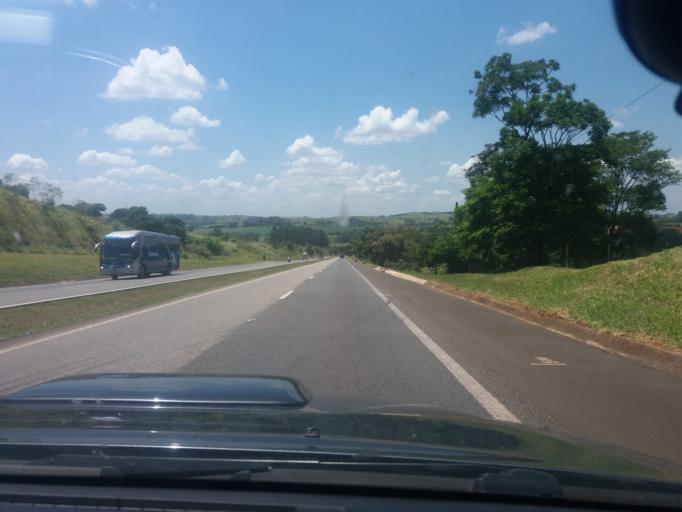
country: BR
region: Sao Paulo
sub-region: Tatui
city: Tatui
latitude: -23.3996
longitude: -47.9256
